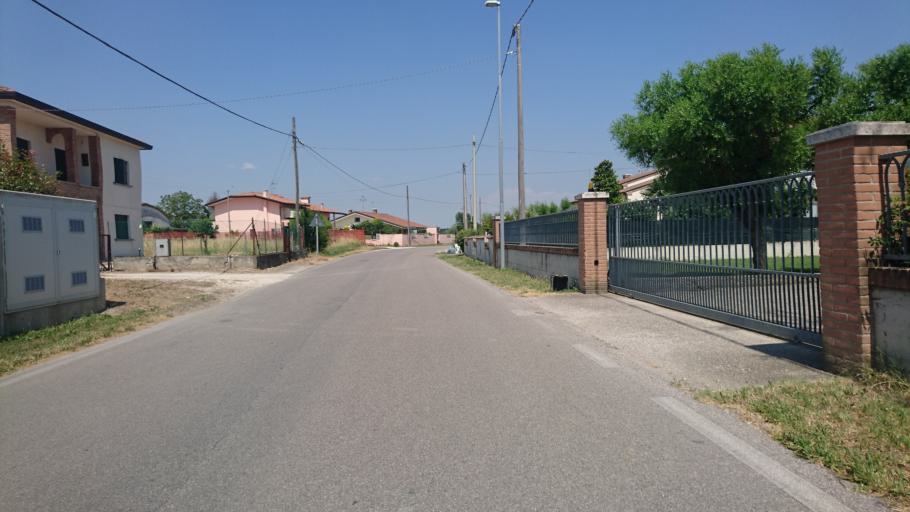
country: IT
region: Veneto
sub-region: Provincia di Padova
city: Solesino
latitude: 45.1721
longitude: 11.7385
